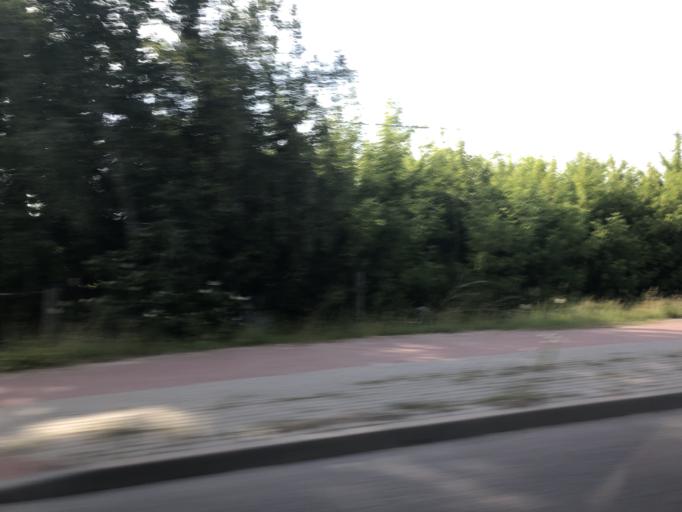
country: PL
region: Podlasie
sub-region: Lomza
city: Lomza
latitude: 53.1569
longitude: 22.0303
